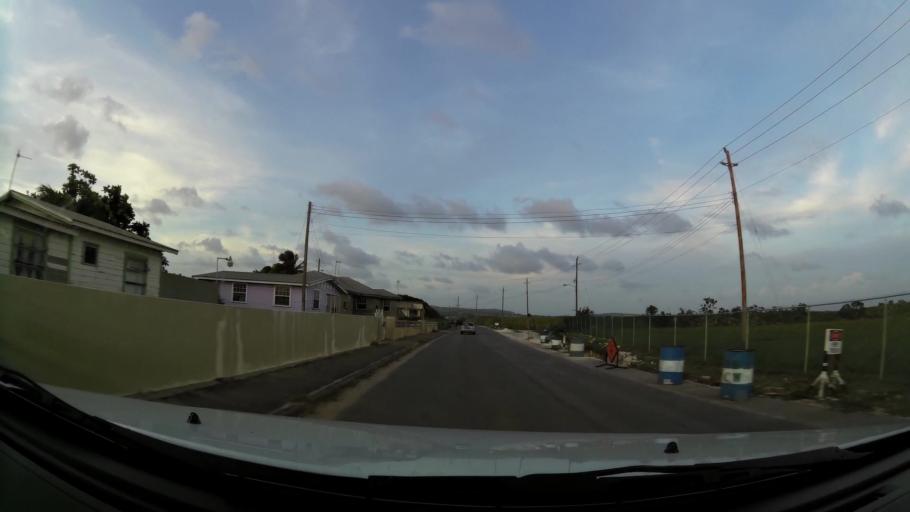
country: BB
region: Saint Philip
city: Crane
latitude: 13.1073
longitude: -59.4850
